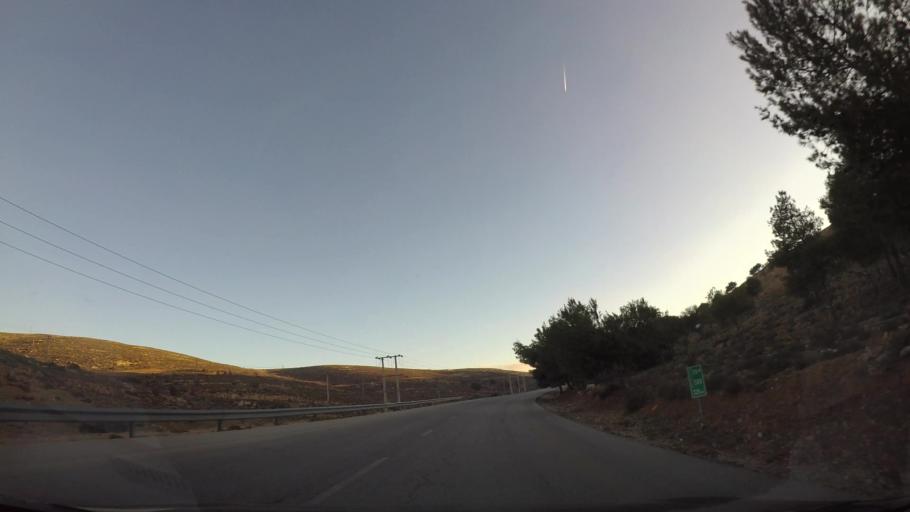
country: JO
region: Ma'an
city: Petra
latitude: 30.4125
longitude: 35.5079
